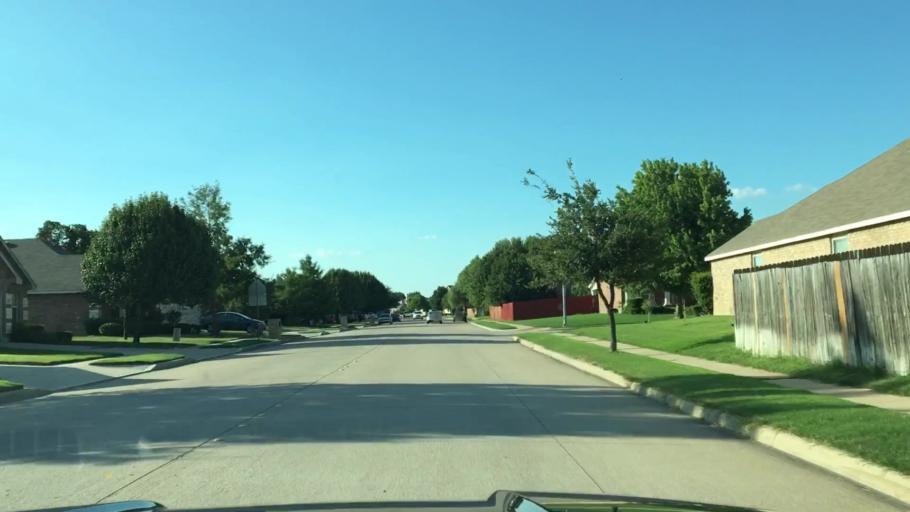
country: US
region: Texas
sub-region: Denton County
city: Justin
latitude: 33.0376
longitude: -97.3192
